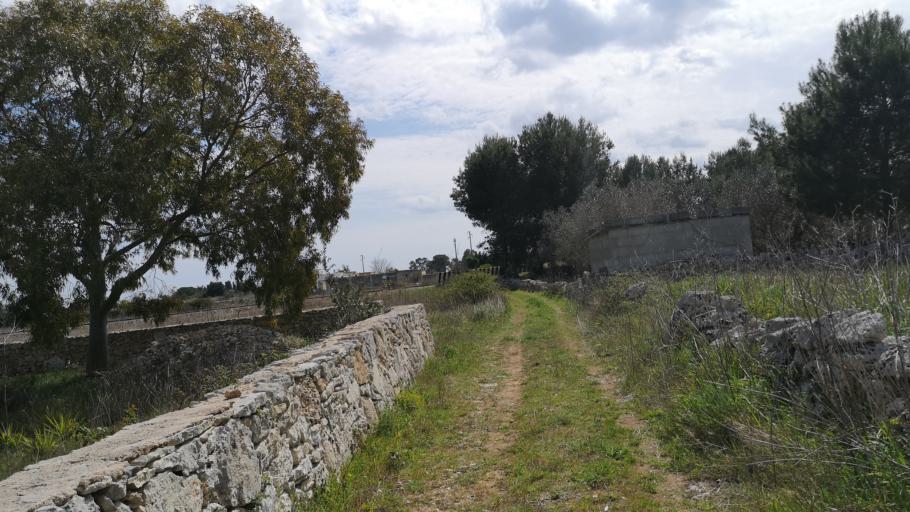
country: IT
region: Apulia
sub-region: Provincia di Lecce
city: Spongano
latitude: 40.0321
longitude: 18.3636
